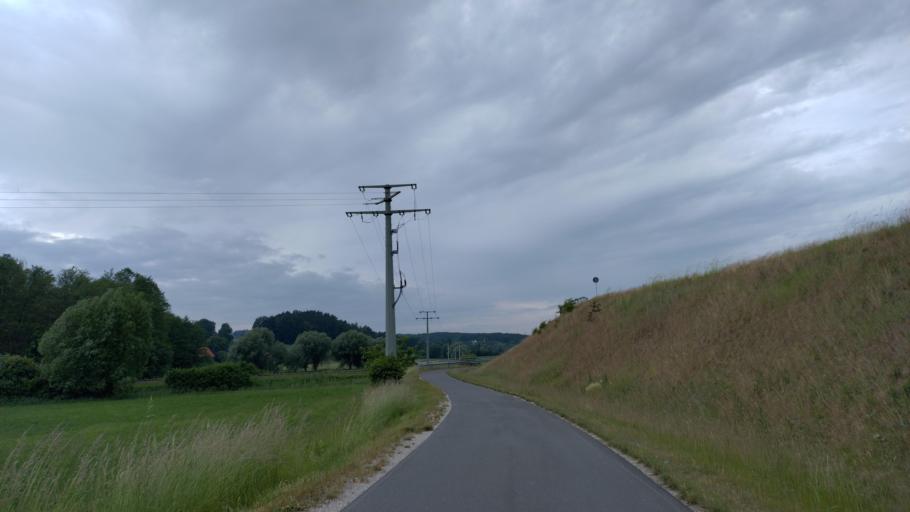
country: DE
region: Bavaria
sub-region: Upper Franconia
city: Bindlach
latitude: 49.9979
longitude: 11.6030
